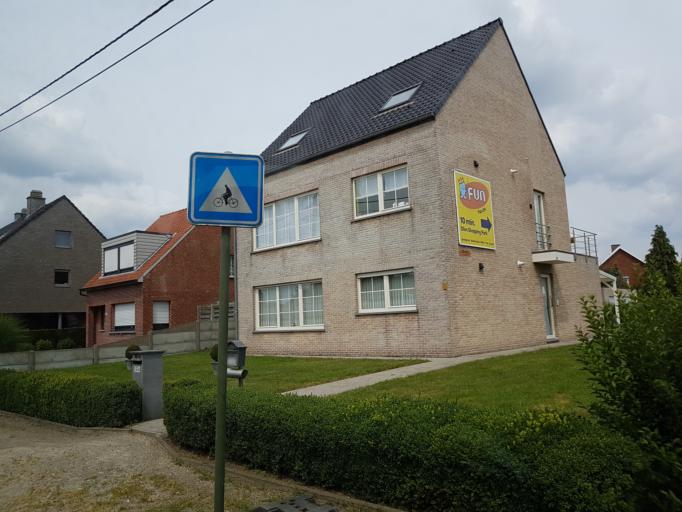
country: BE
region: Flanders
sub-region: Provincie Antwerpen
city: Olen
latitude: 51.1071
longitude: 4.8696
